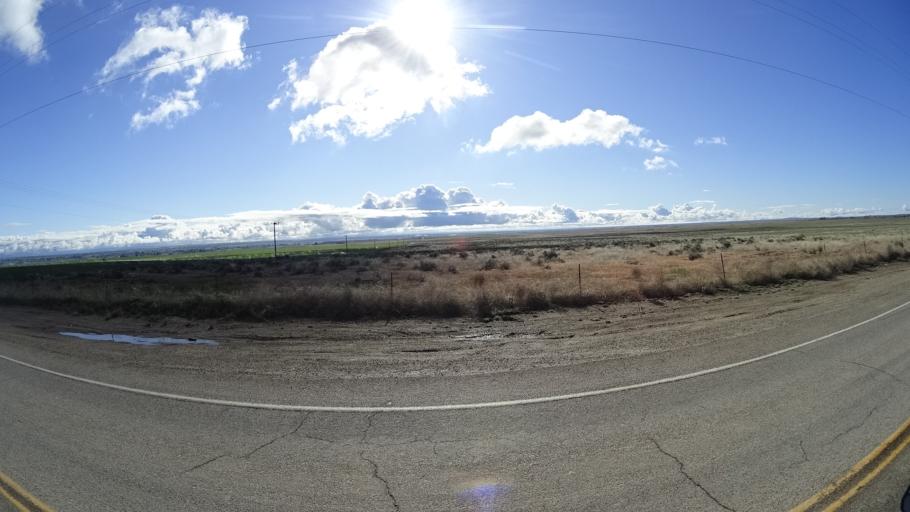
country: US
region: Idaho
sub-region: Ada County
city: Kuna
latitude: 43.4442
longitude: -116.4138
